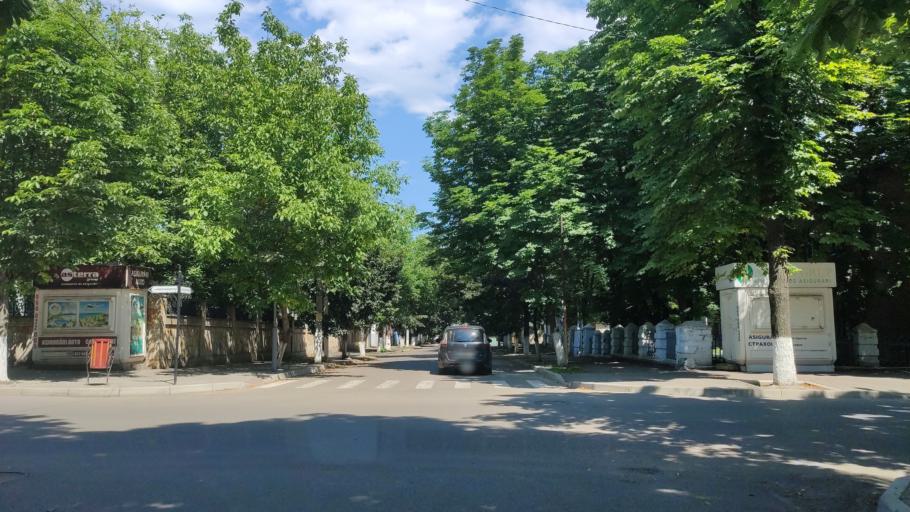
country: MD
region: Raionul Soroca
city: Soroca
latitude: 48.1515
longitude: 28.3020
